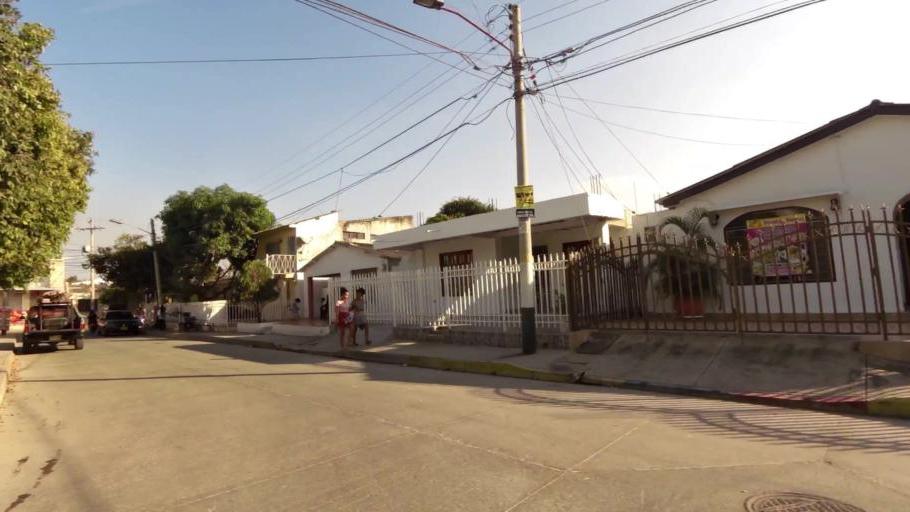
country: CO
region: Bolivar
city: Cartagena
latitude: 10.3851
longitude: -75.4830
